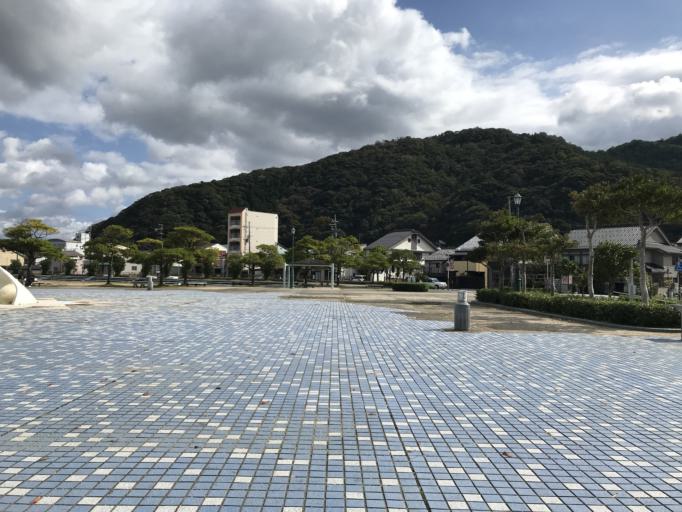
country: JP
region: Fukui
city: Obama
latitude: 35.4930
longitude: 135.7342
